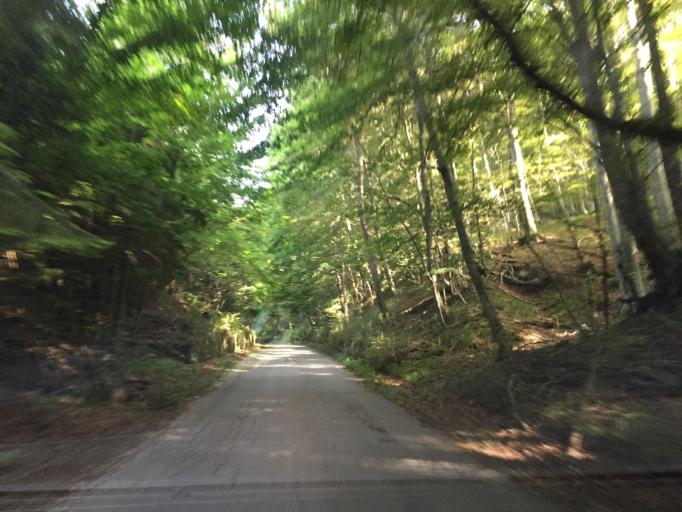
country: HR
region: Primorsko-Goranska
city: Klana
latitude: 45.4729
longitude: 14.4238
